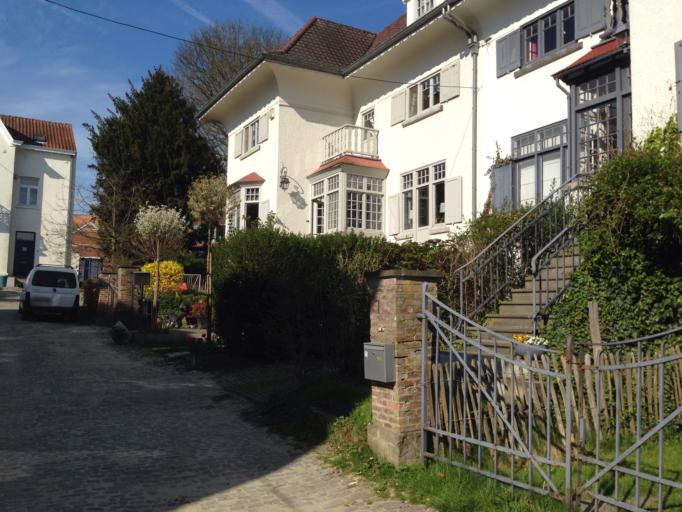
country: BE
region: Flanders
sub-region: Provincie Vlaams-Brabant
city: Dilbeek
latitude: 50.8626
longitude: 4.2986
